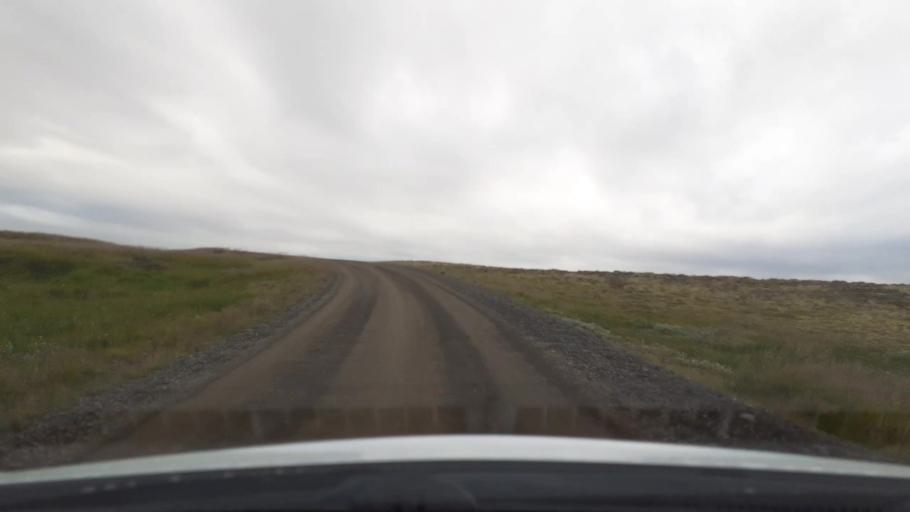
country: IS
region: Capital Region
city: Mosfellsbaer
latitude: 64.1976
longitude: -21.5559
